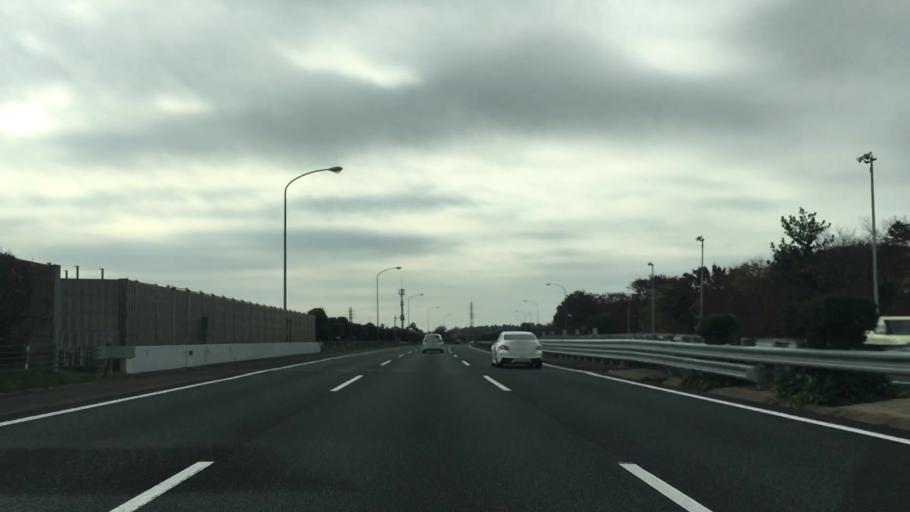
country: JP
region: Chiba
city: Narita
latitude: 35.7462
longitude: 140.3135
